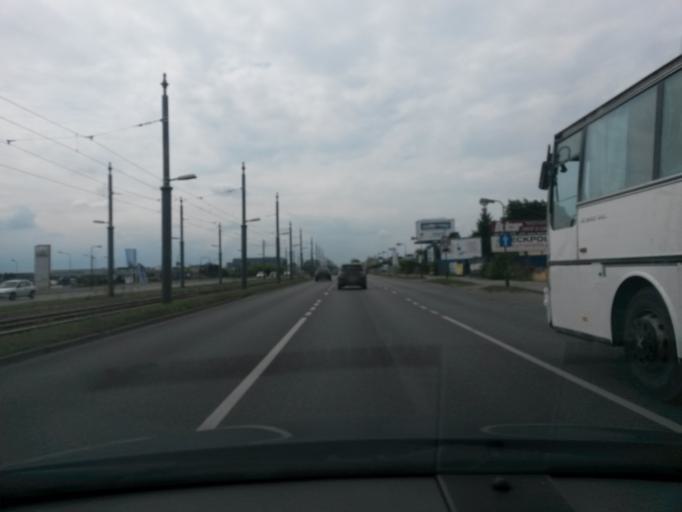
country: PL
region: Masovian Voivodeship
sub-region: Warszawa
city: Wlochy
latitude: 52.1845
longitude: 20.9528
